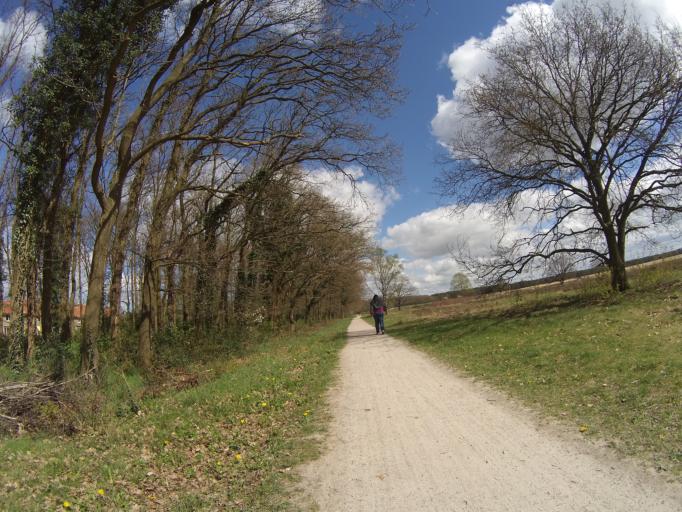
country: NL
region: North Holland
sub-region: Gemeente Bussum
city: Bussum
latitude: 52.2622
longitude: 5.1753
